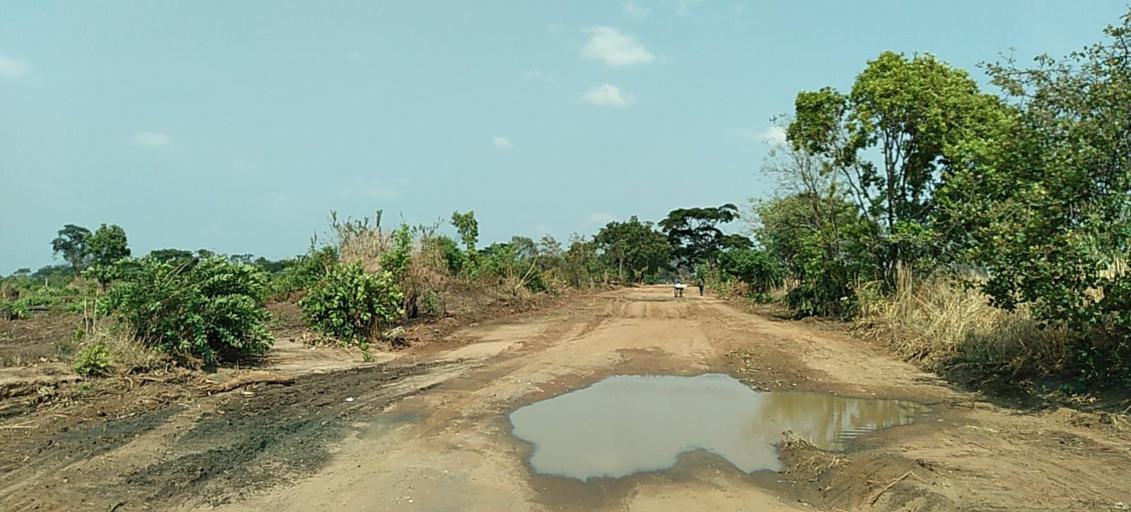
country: ZM
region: Copperbelt
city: Luanshya
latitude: -13.0893
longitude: 28.2628
